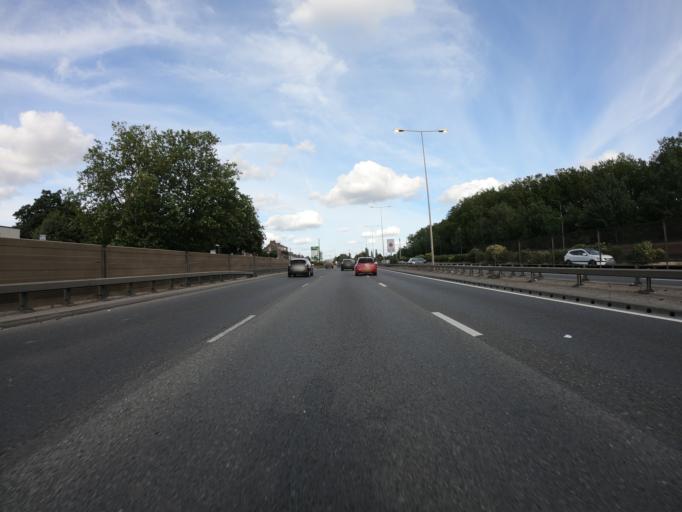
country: GB
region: England
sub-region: Greater London
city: East Ham
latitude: 51.5173
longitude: 0.0260
